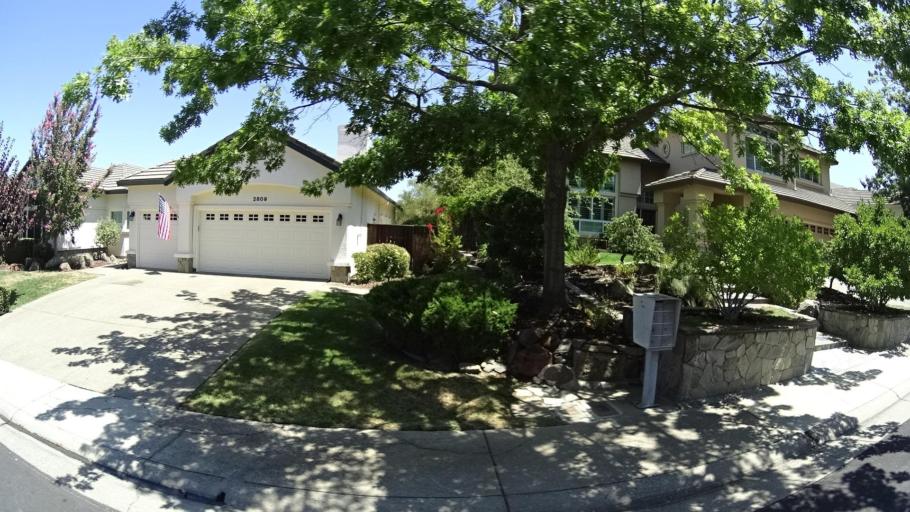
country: US
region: California
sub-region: Placer County
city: Rocklin
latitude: 38.8234
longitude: -121.2458
